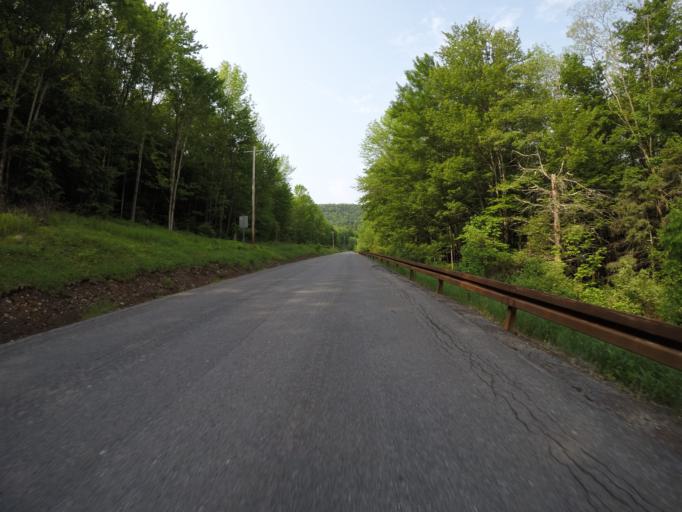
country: US
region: New York
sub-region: Sullivan County
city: Livingston Manor
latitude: 42.1043
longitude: -74.7743
